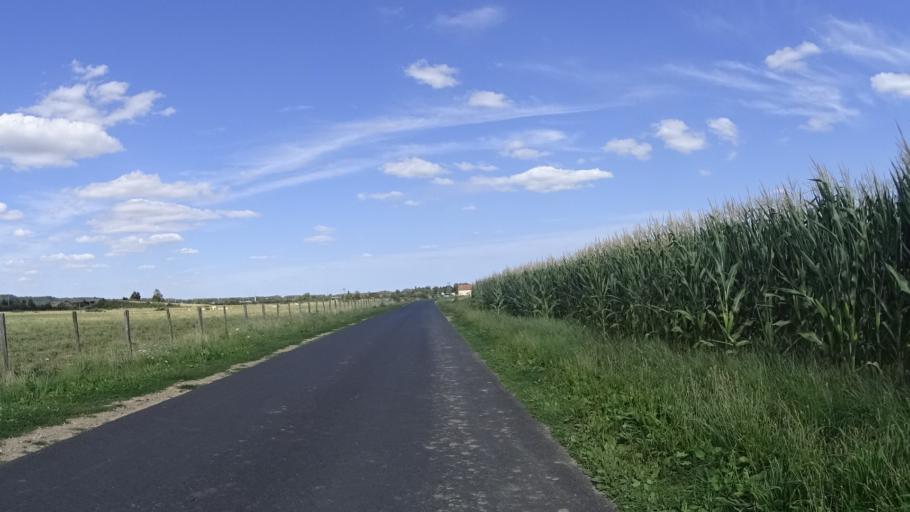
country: FR
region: Centre
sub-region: Departement d'Indre-et-Loire
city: Nazelles-Negron
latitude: 47.4110
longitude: 0.9400
